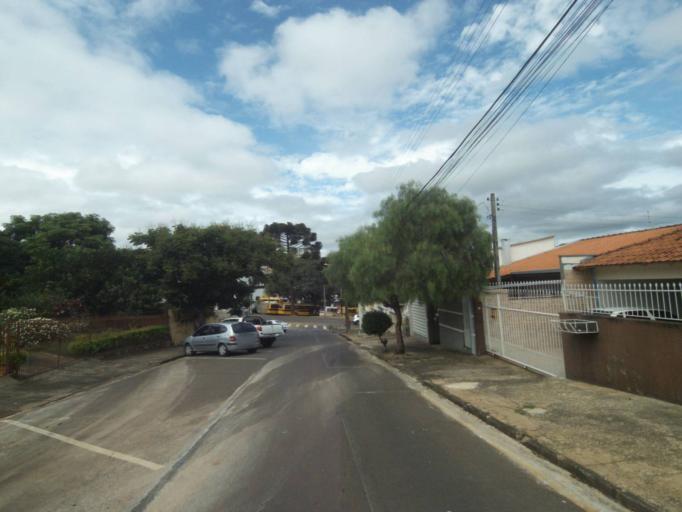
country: BR
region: Parana
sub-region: Telemaco Borba
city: Telemaco Borba
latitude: -24.3300
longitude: -50.6256
